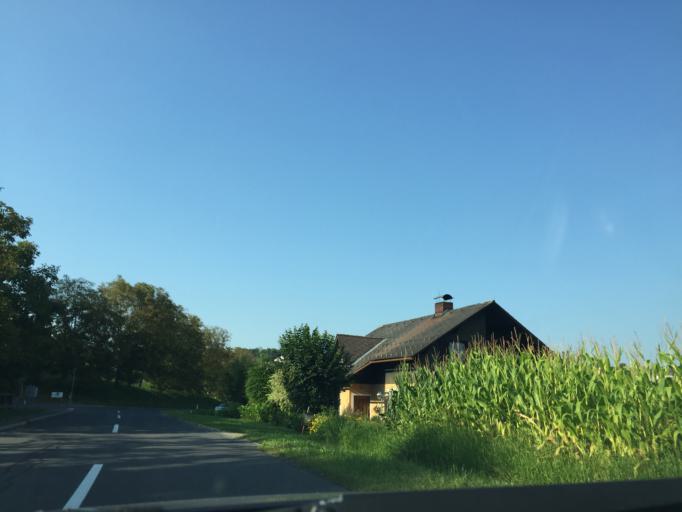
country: AT
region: Styria
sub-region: Politischer Bezirk Suedoststeiermark
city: Straden
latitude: 46.8043
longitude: 15.8606
